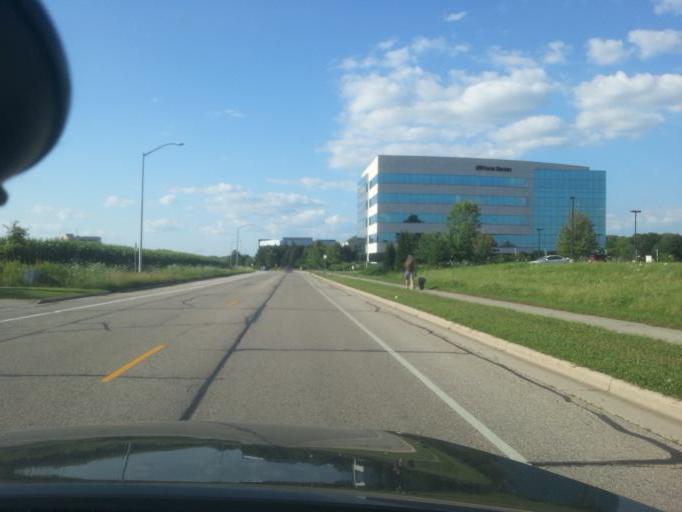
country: US
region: Wisconsin
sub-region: Dane County
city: Middleton
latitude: 43.0834
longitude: -89.5240
